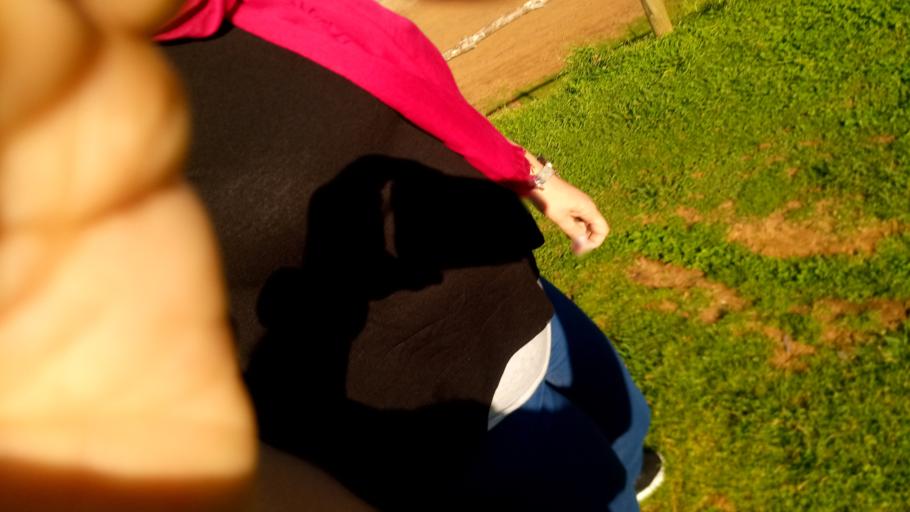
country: PT
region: Azores
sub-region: Angra do Heroismo
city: Angra do Heroismo
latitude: 38.6802
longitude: -27.3153
